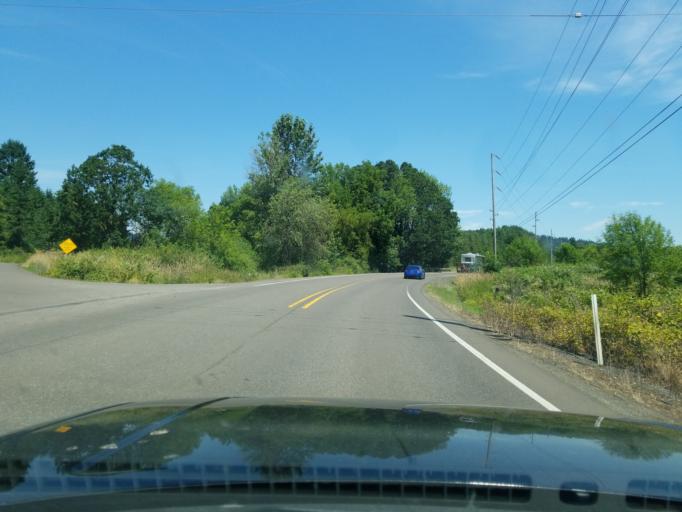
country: US
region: Oregon
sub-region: Yamhill County
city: Yamhill
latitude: 45.3616
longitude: -123.1686
